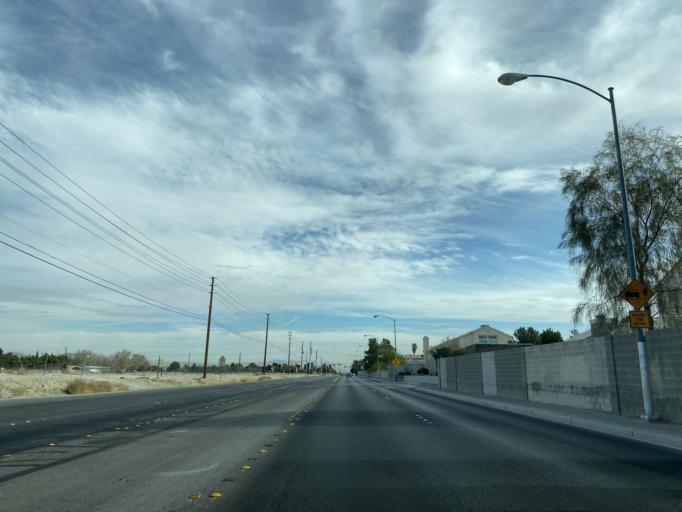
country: US
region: Nevada
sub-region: Clark County
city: North Las Vegas
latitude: 36.2468
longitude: -115.1935
